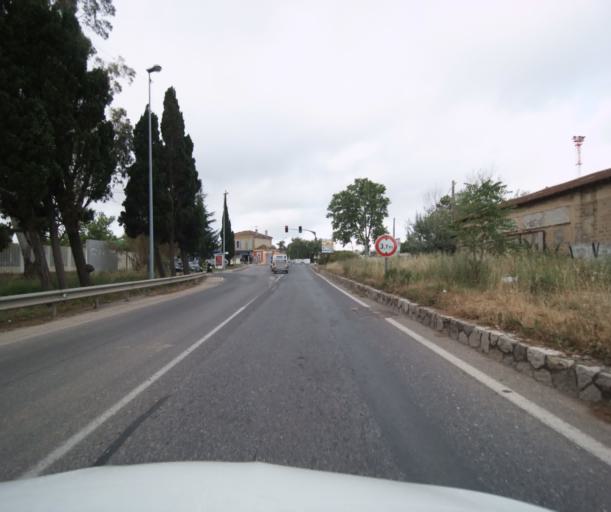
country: FR
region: Provence-Alpes-Cote d'Azur
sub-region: Departement du Var
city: La Seyne-sur-Mer
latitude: 43.1175
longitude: 5.8789
